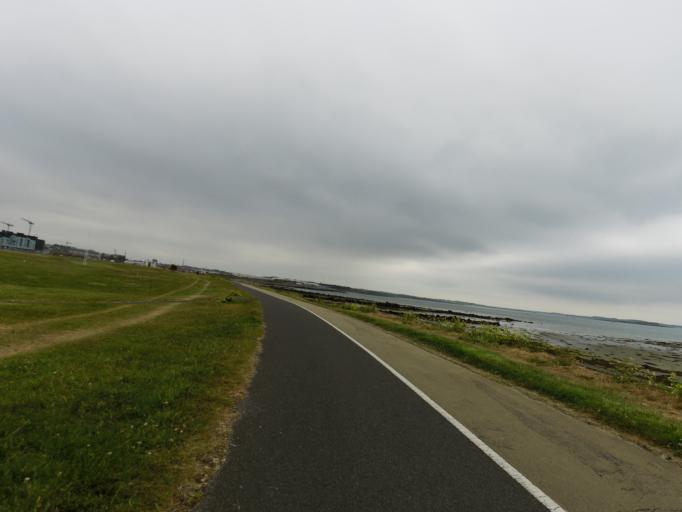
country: IE
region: Connaught
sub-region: County Galway
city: Gaillimh
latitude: 53.2640
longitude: -9.0528
